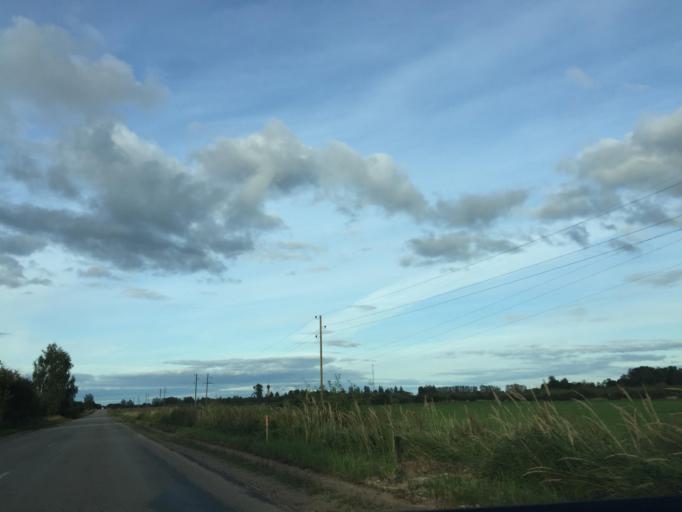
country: LV
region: Nereta
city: Nereta
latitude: 56.2715
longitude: 25.3774
